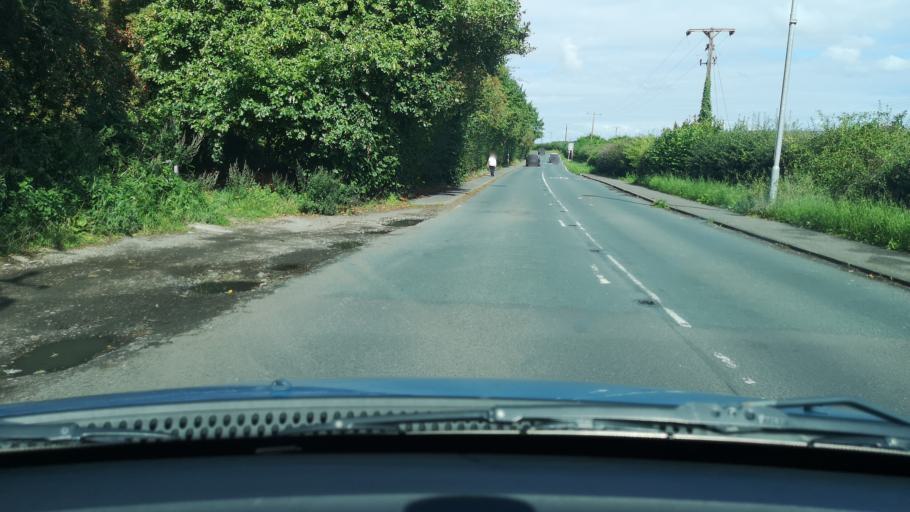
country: GB
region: England
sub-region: City and Borough of Wakefield
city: Crigglestone
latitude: 53.6486
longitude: -1.5129
